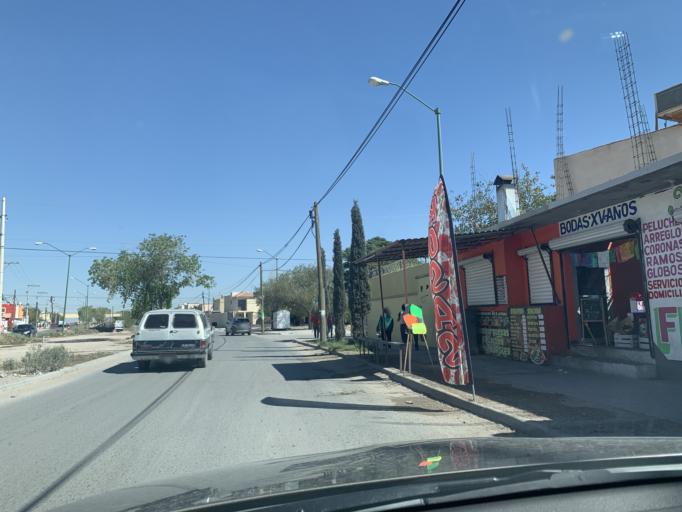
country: US
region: Texas
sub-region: El Paso County
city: Socorro Mission Number 1 Colonia
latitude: 31.6021
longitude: -106.3559
